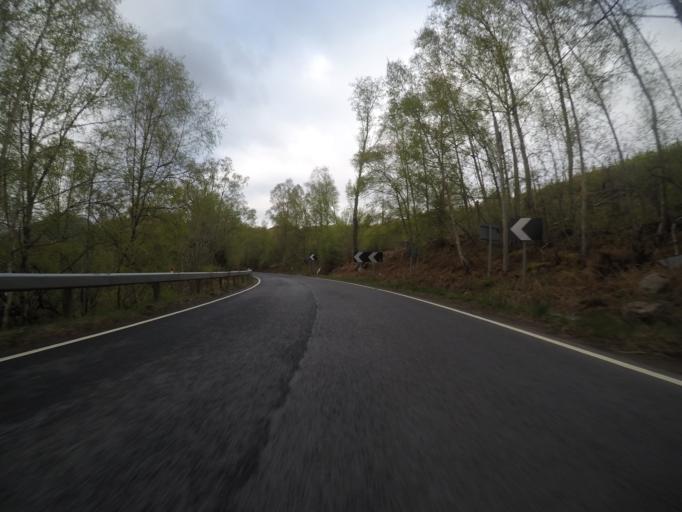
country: GB
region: Scotland
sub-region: Highland
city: Kingussie
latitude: 56.9640
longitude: -4.4522
